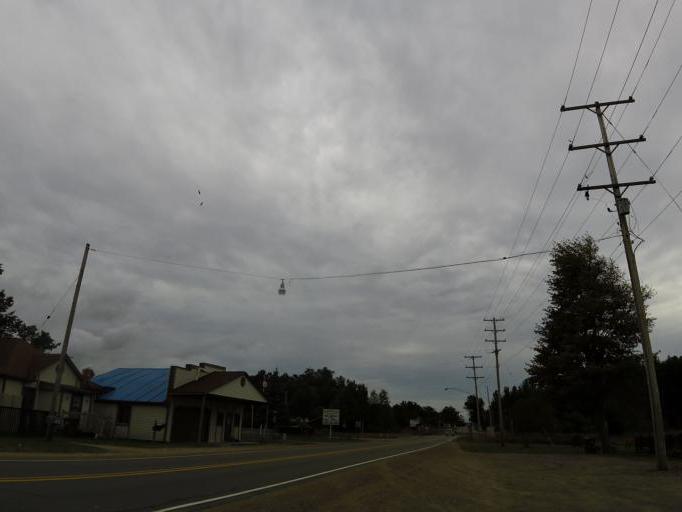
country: US
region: Michigan
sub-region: Roscommon County
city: Saint Helen
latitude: 44.3749
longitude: -84.4104
